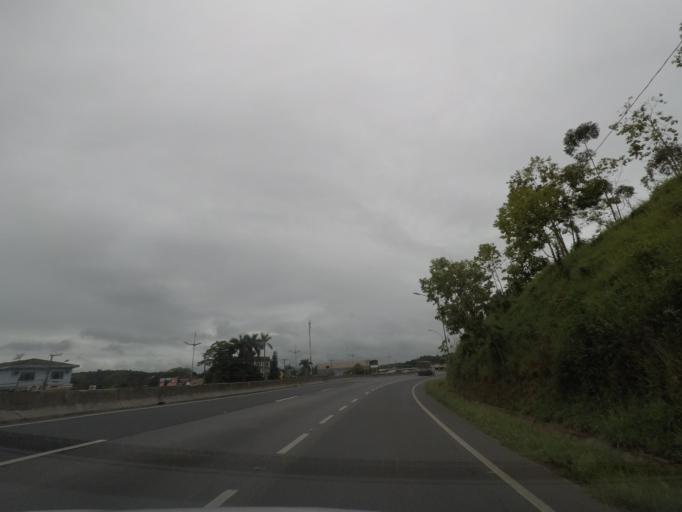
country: BR
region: Sao Paulo
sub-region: Cajati
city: Cajati
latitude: -24.7302
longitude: -48.1074
